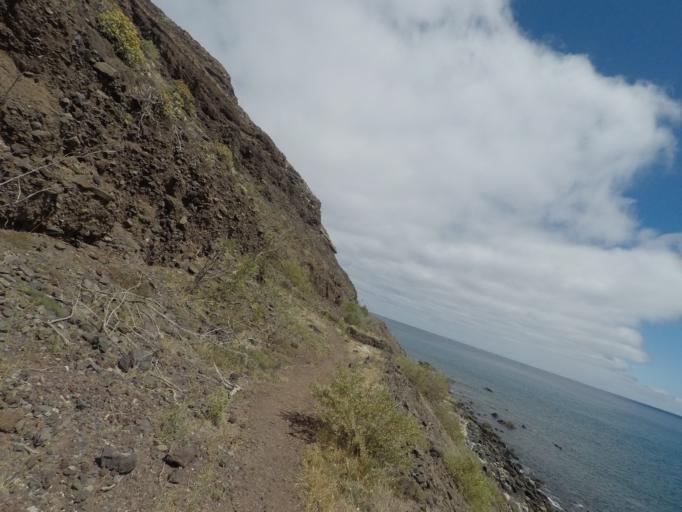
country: PT
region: Madeira
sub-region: Porto Santo
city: Vila de Porto Santo
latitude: 33.0610
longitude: -16.3011
